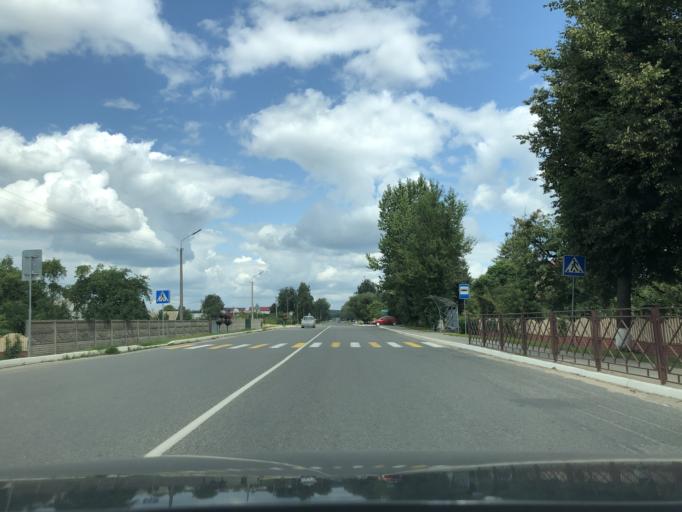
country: BY
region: Minsk
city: Lahoysk
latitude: 54.2109
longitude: 27.8518
